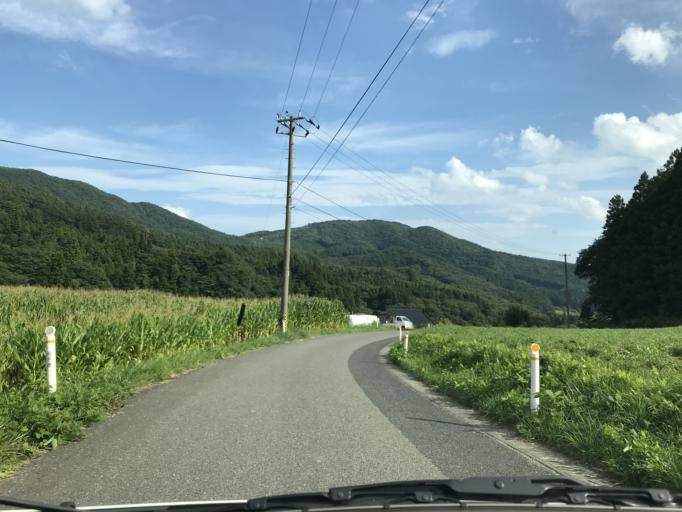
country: JP
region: Iwate
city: Ofunato
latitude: 38.9650
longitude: 141.4720
